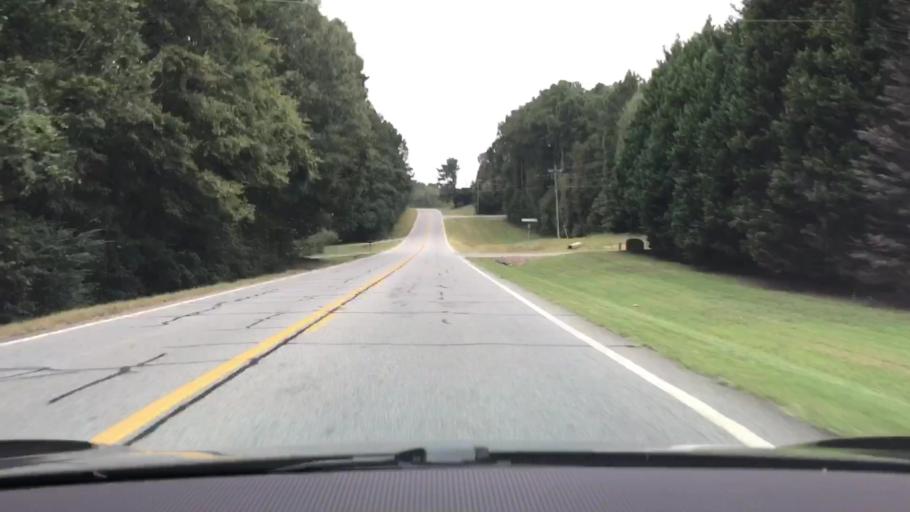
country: US
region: Georgia
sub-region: Oconee County
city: Watkinsville
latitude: 33.7765
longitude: -83.3110
